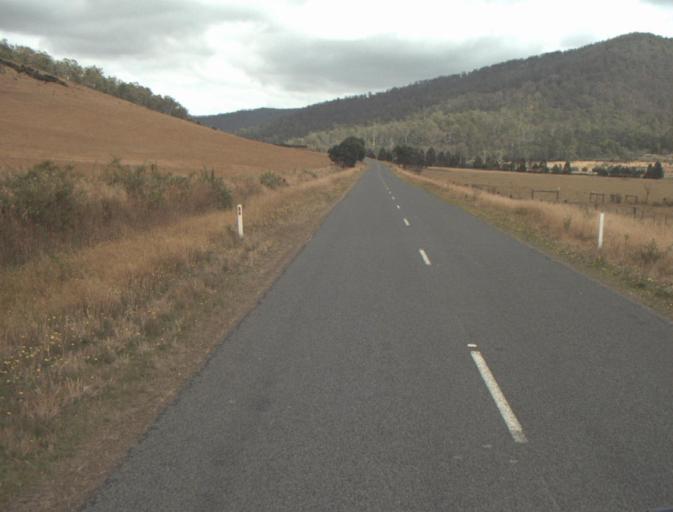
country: AU
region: Tasmania
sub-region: Northern Midlands
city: Evandale
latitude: -41.4971
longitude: 147.4515
